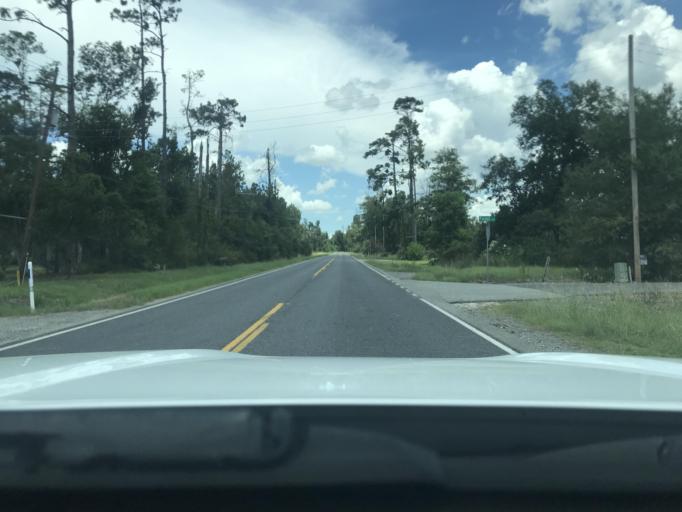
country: US
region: Louisiana
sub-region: Calcasieu Parish
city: Moss Bluff
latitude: 30.2797
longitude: -93.1681
